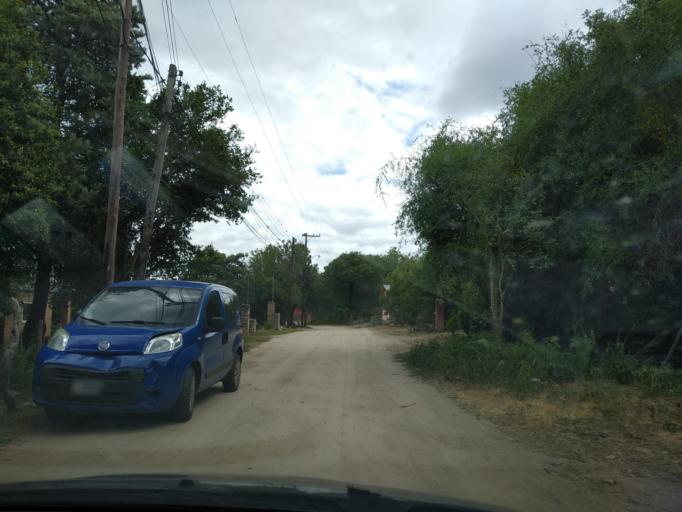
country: AR
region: Cordoba
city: Villa Las Rosas
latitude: -31.9413
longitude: -65.0308
